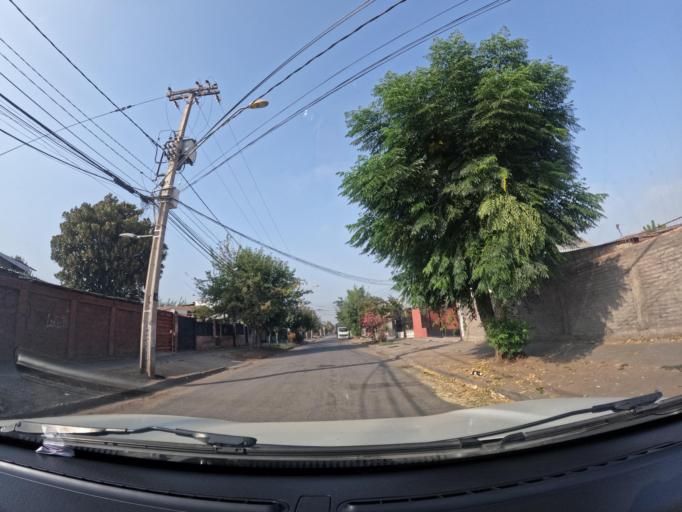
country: CL
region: Santiago Metropolitan
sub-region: Provincia de Santiago
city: Villa Presidente Frei, Nunoa, Santiago, Chile
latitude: -33.4731
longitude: -70.5605
